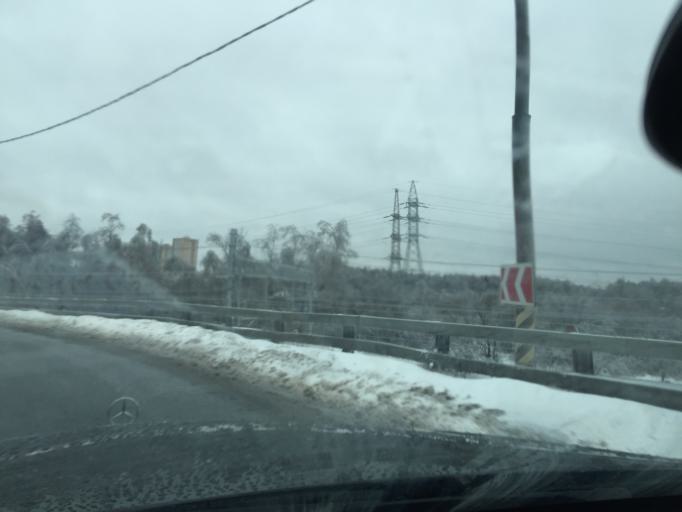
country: RU
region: Moscow
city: Khimki
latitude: 55.9205
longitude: 37.3916
